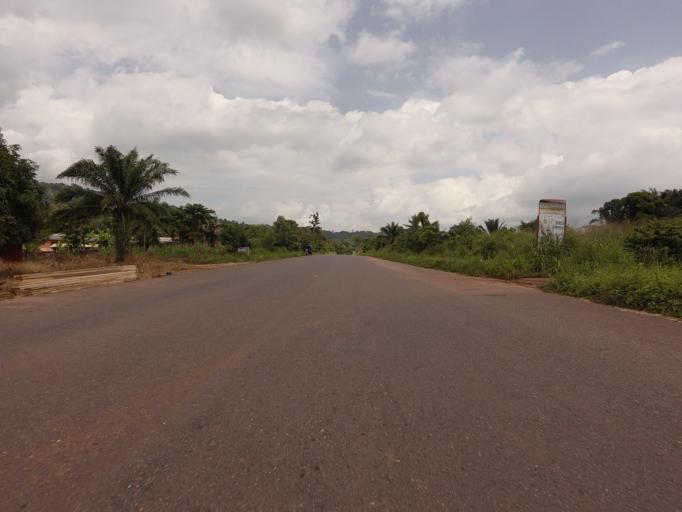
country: GH
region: Volta
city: Ho
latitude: 6.5191
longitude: 0.2195
